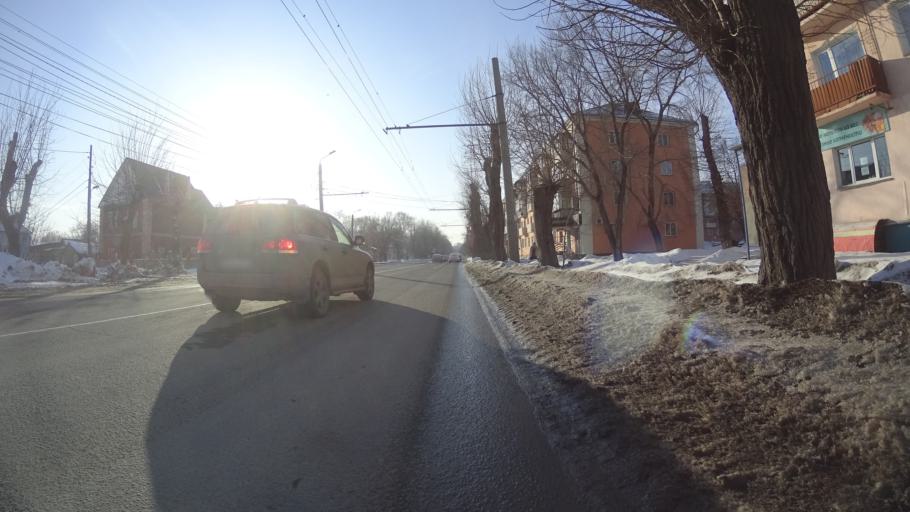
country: RU
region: Chelyabinsk
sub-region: Gorod Chelyabinsk
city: Chelyabinsk
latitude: 55.1817
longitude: 61.4480
